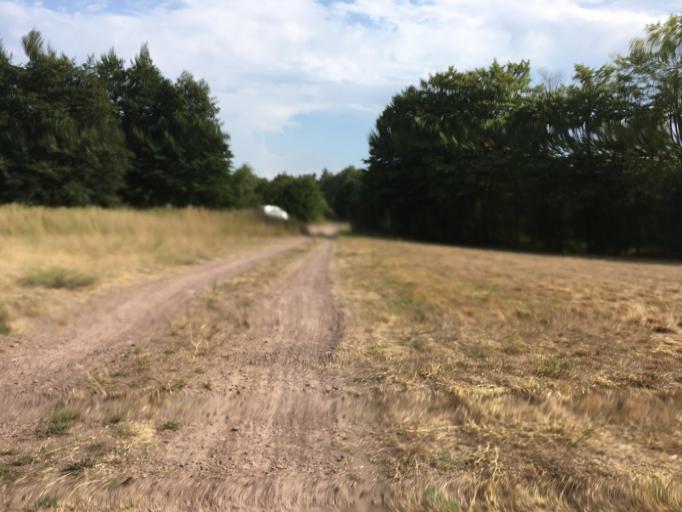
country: DE
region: Brandenburg
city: Zehdenick
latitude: 53.0506
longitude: 13.2940
